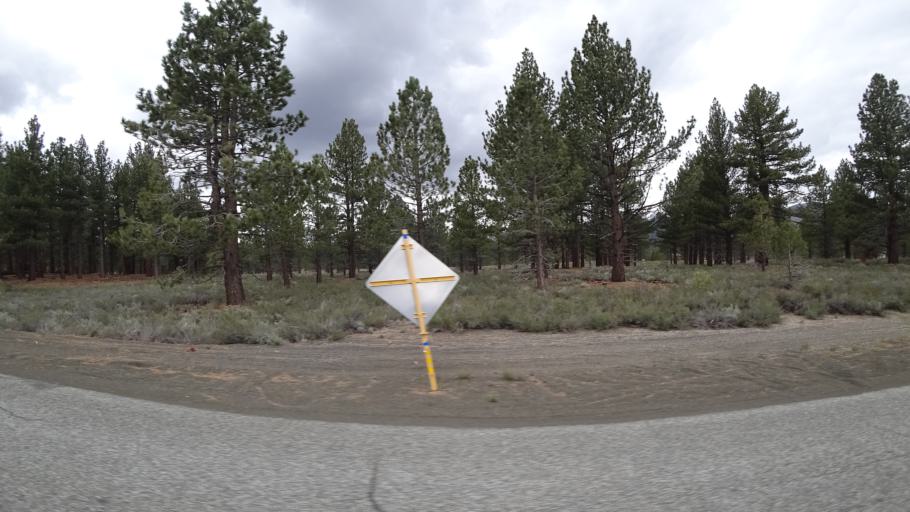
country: US
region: California
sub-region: Mono County
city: Mammoth Lakes
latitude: 37.7342
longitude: -118.9701
